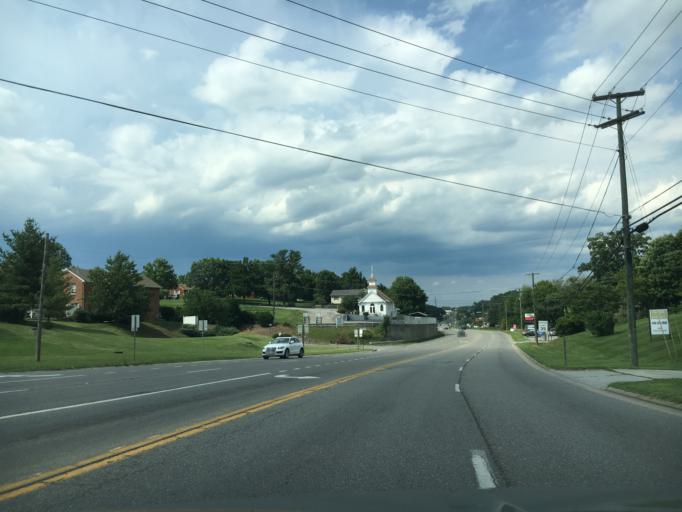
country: US
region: Virginia
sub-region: Roanoke County
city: Cave Spring
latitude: 37.2178
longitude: -80.0174
